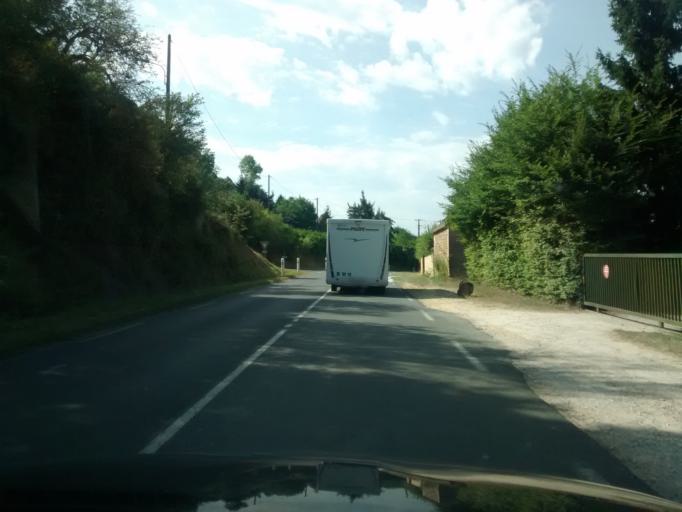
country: FR
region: Aquitaine
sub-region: Departement de la Dordogne
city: Cenac-et-Saint-Julien
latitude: 44.8412
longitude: 1.1709
